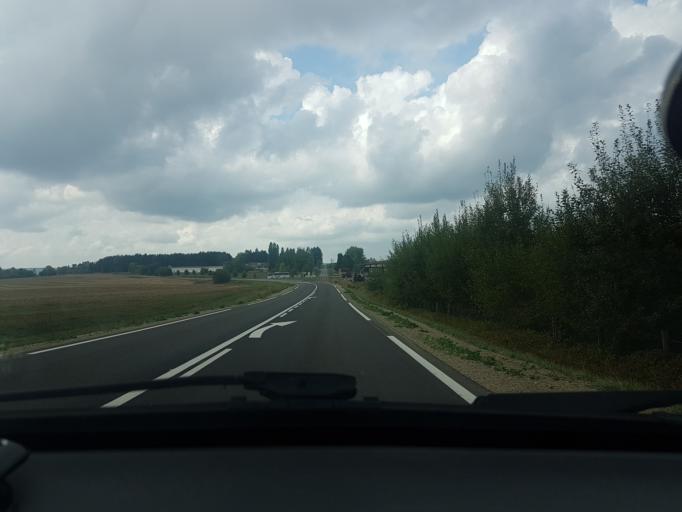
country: FR
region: Franche-Comte
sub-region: Departement de la Haute-Saone
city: Villersexel
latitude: 47.5486
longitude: 6.4491
